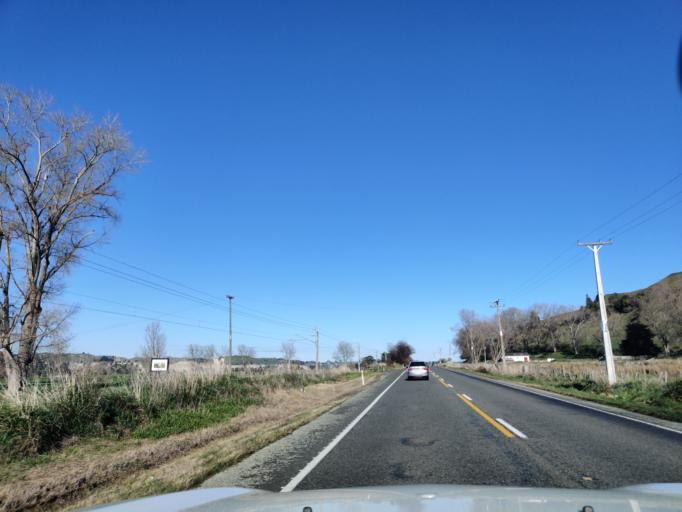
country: NZ
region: Manawatu-Wanganui
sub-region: Ruapehu District
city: Waiouru
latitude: -39.8502
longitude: 175.7336
